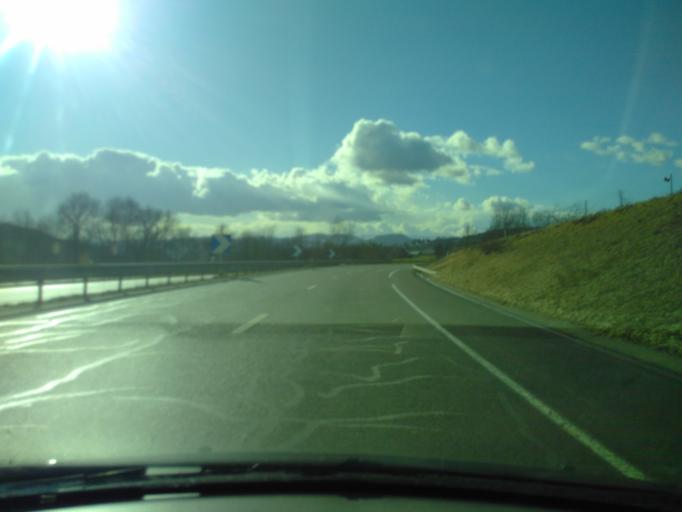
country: FR
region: Rhone-Alpes
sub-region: Departement de la Haute-Savoie
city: Evires
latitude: 46.0251
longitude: 6.2264
